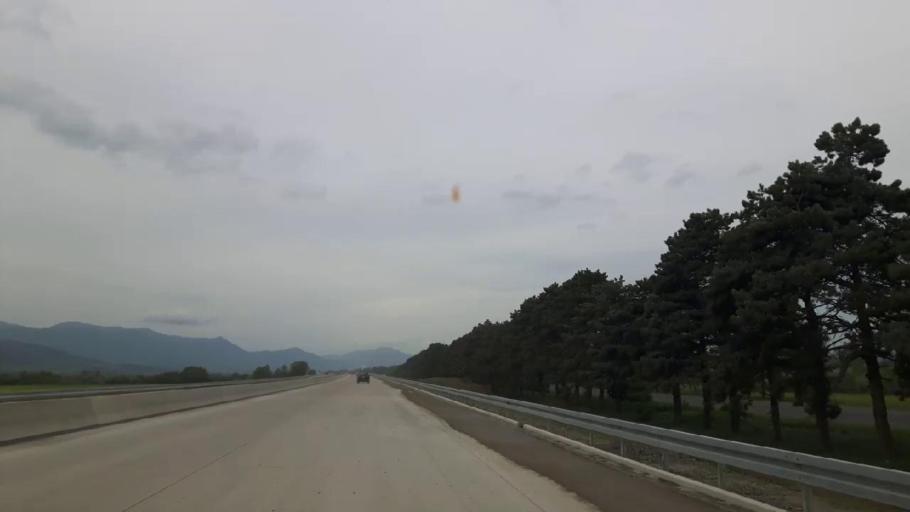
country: GE
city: Agara
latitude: 42.0206
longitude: 43.7444
